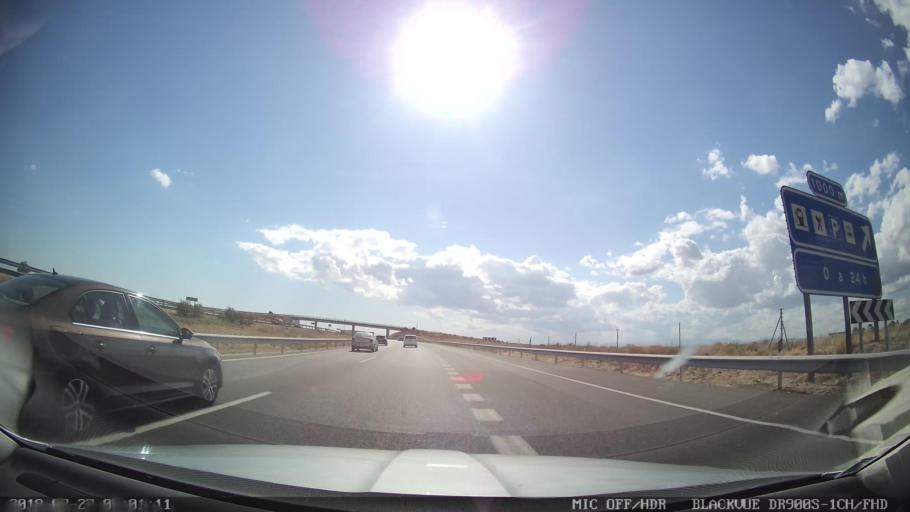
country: ES
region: Castille-La Mancha
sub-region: Province of Toledo
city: Las Ventas de Retamosa
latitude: 40.1880
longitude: -4.1257
